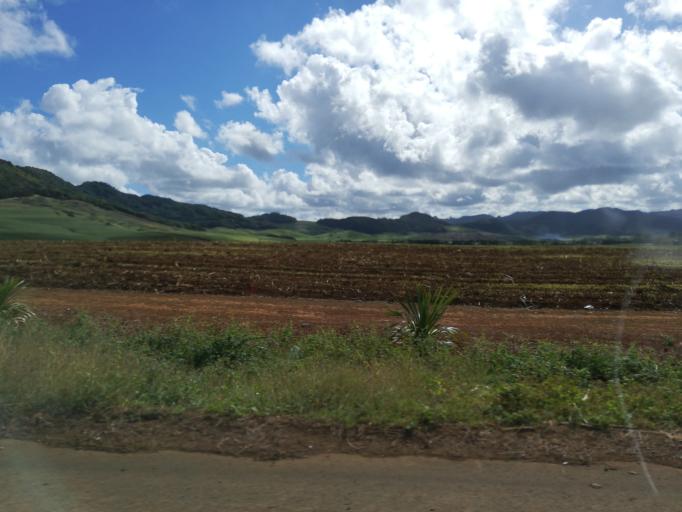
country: MU
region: Grand Port
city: Mahebourg
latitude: -20.3762
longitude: 57.6993
